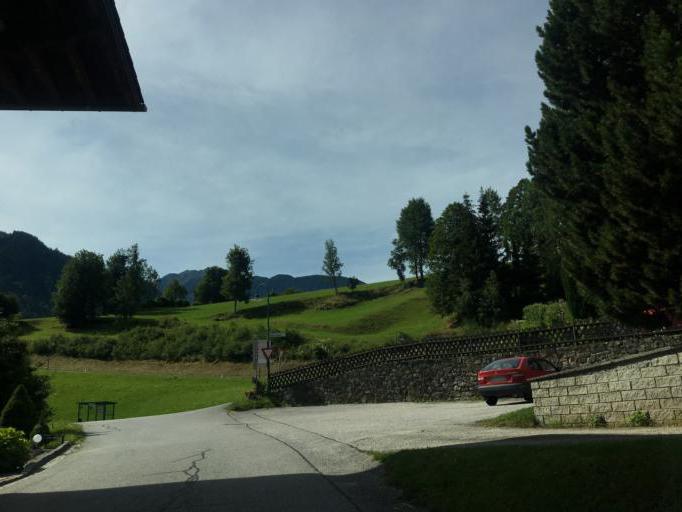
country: AT
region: Styria
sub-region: Politischer Bezirk Liezen
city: Schladming
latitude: 47.3861
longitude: 13.6754
